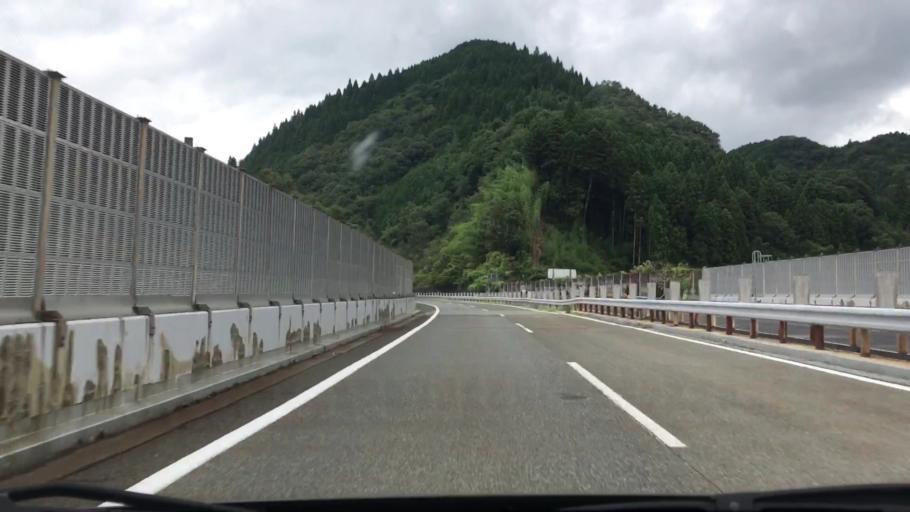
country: JP
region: Okayama
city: Niimi
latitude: 35.0126
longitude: 133.4338
